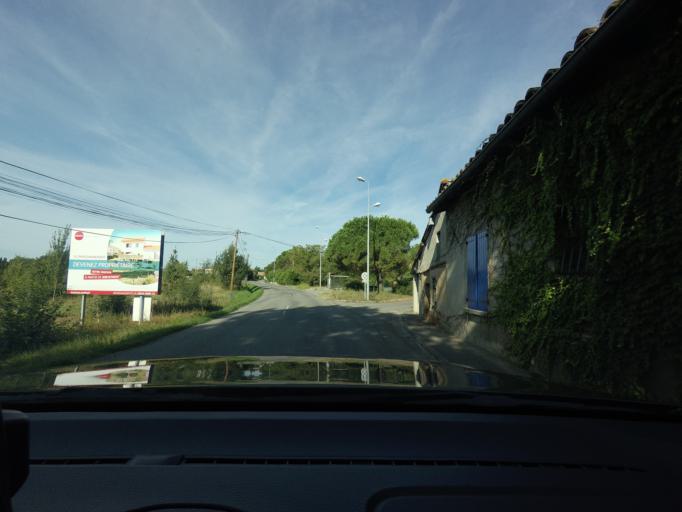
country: FR
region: Midi-Pyrenees
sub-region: Departement de la Haute-Garonne
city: Cornebarrieu
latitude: 43.6426
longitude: 1.3186
